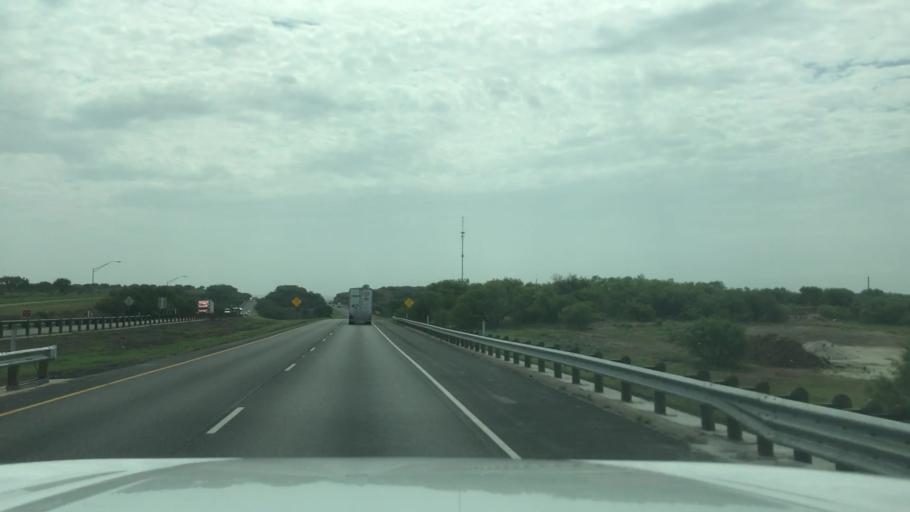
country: US
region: Texas
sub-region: Callahan County
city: Baird
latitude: 32.3980
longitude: -99.3734
